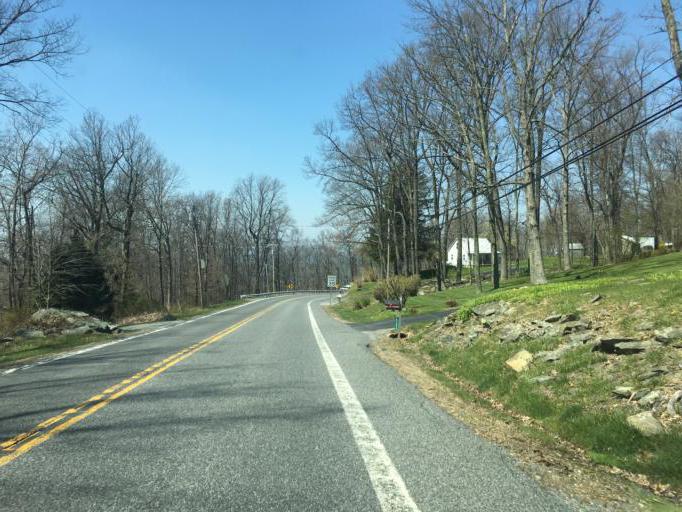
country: US
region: Maryland
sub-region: Washington County
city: Smithsburg
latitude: 39.6373
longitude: -77.5461
